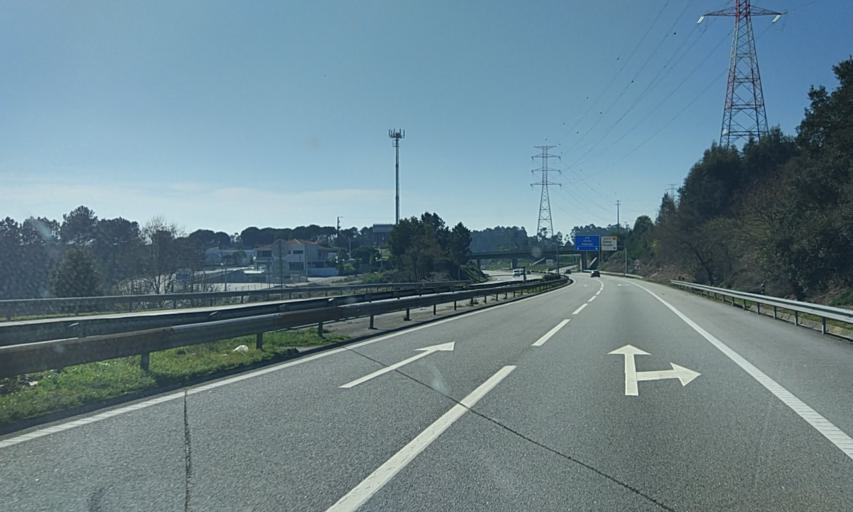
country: PT
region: Porto
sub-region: Paredes
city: Baltar
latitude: 41.1726
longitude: -8.3847
